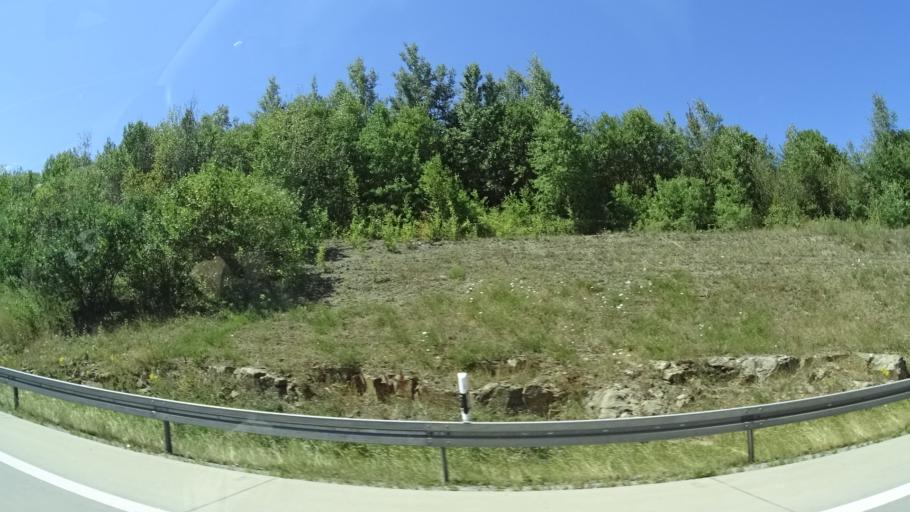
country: DE
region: Bavaria
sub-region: Regierungsbezirk Unterfranken
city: Rodelmaier
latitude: 50.3209
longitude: 10.2884
